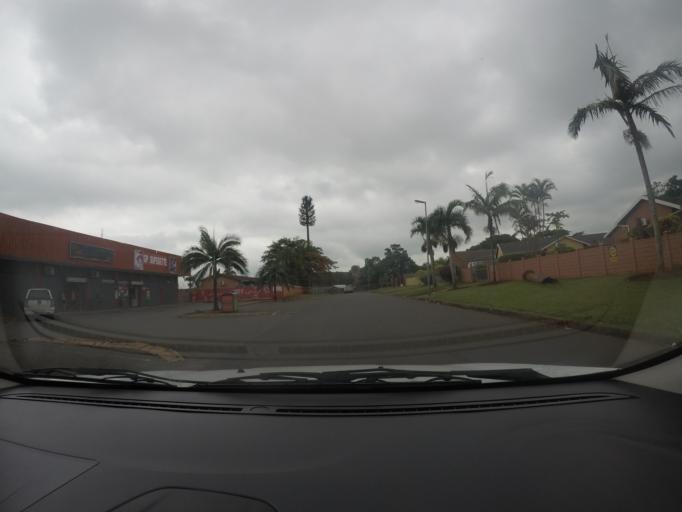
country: ZA
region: KwaZulu-Natal
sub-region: uThungulu District Municipality
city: Empangeni
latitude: -28.7664
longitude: 31.8979
